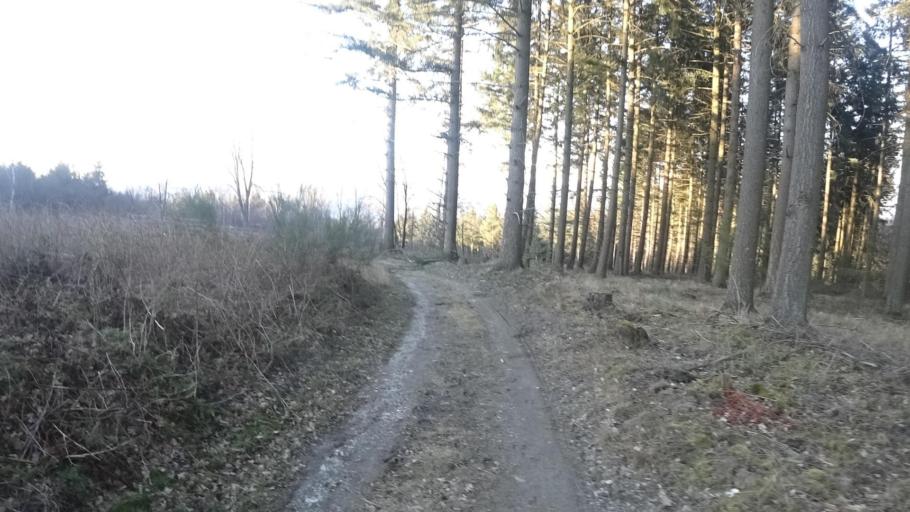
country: DE
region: Rheinland-Pfalz
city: Kamp-Bornhofen
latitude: 50.2017
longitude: 7.5928
